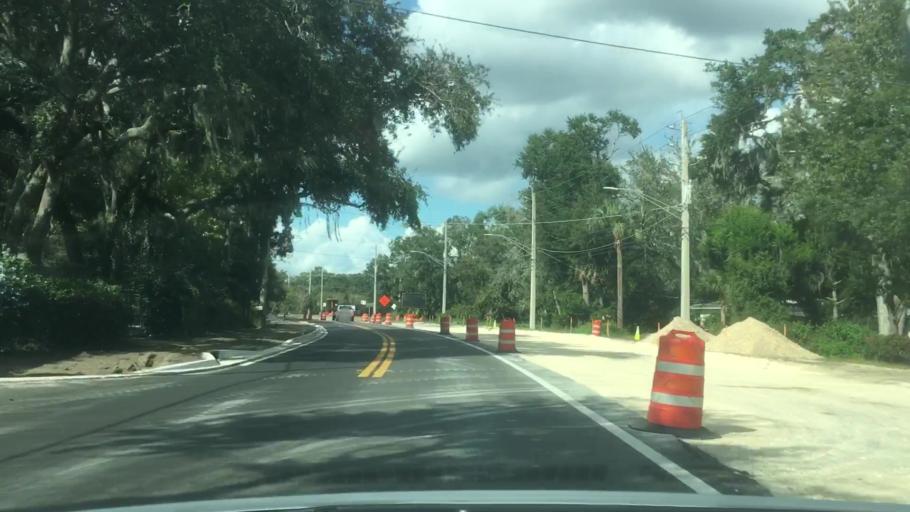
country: US
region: Florida
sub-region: Duval County
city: Atlantic Beach
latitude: 30.3559
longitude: -81.4616
